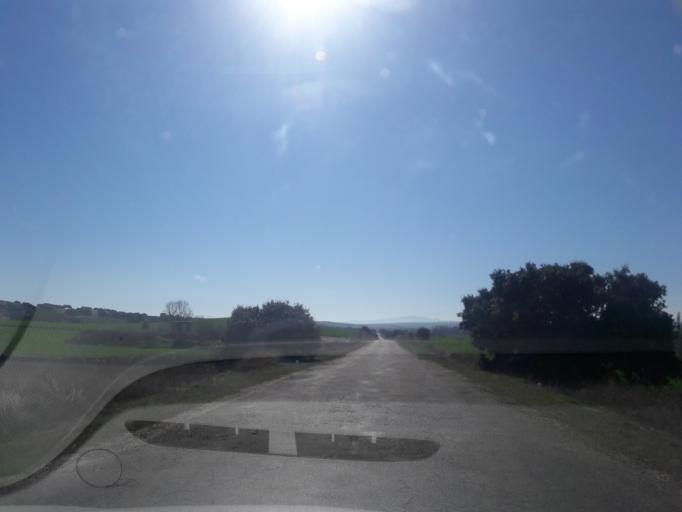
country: ES
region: Castille and Leon
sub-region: Provincia de Salamanca
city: Mancera de Abajo
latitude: 40.8229
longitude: -5.1769
